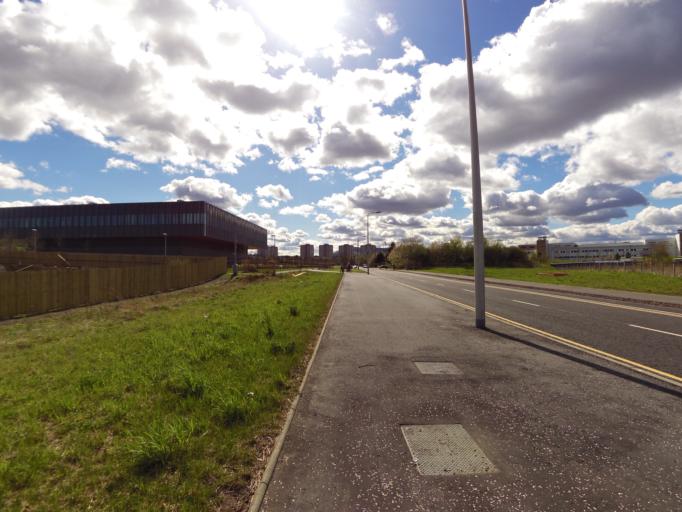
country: GB
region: Scotland
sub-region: West Lothian
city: Seafield
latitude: 55.9224
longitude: -3.1294
